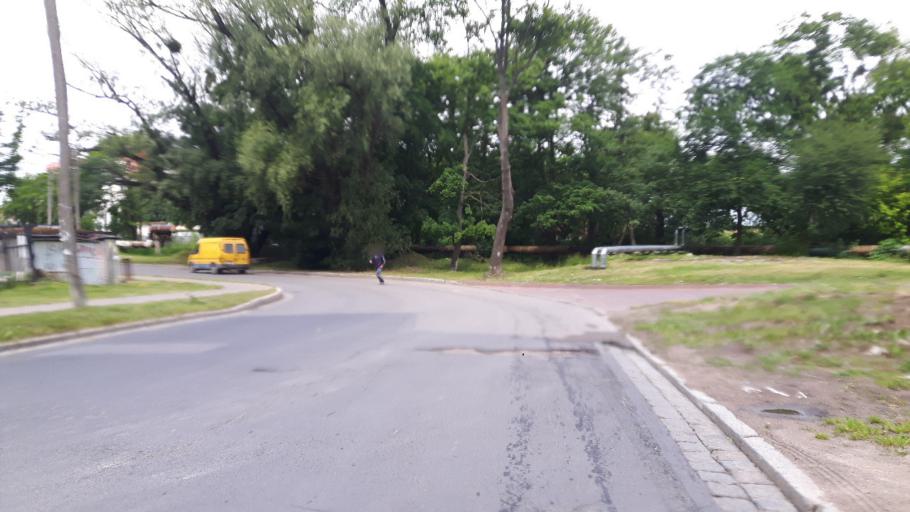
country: RU
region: Kaliningrad
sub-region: Gorod Kaliningrad
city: Kaliningrad
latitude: 54.7348
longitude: 20.5165
